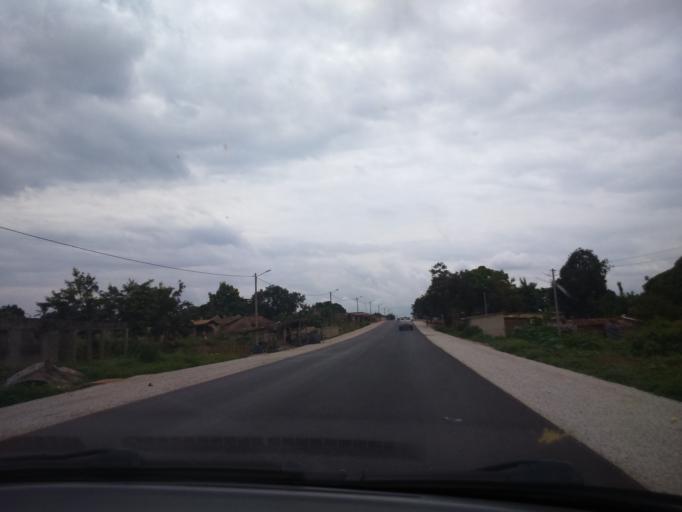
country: CI
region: Lagunes
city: Akoupe
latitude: 6.3384
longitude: -3.8522
